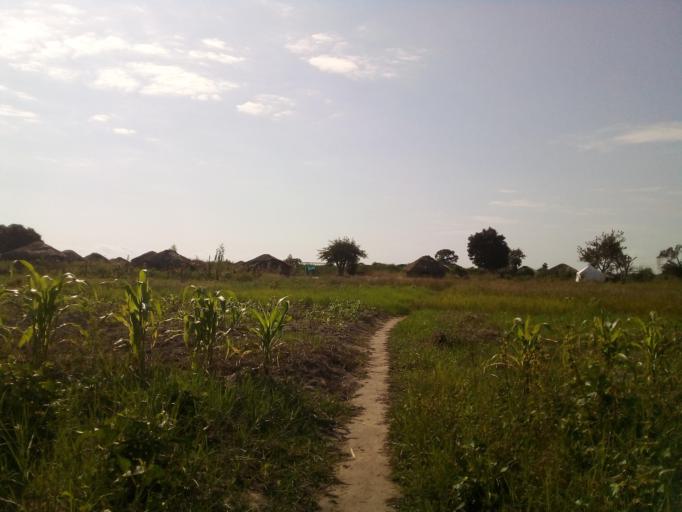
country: MZ
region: Zambezia
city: Quelimane
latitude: -17.5535
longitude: 36.7052
